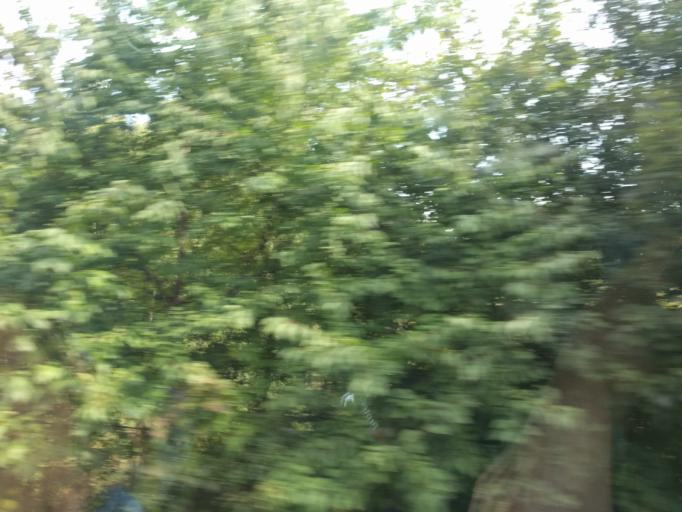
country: DE
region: Schleswig-Holstein
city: Reinfeld
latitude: 53.8325
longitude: 10.4991
